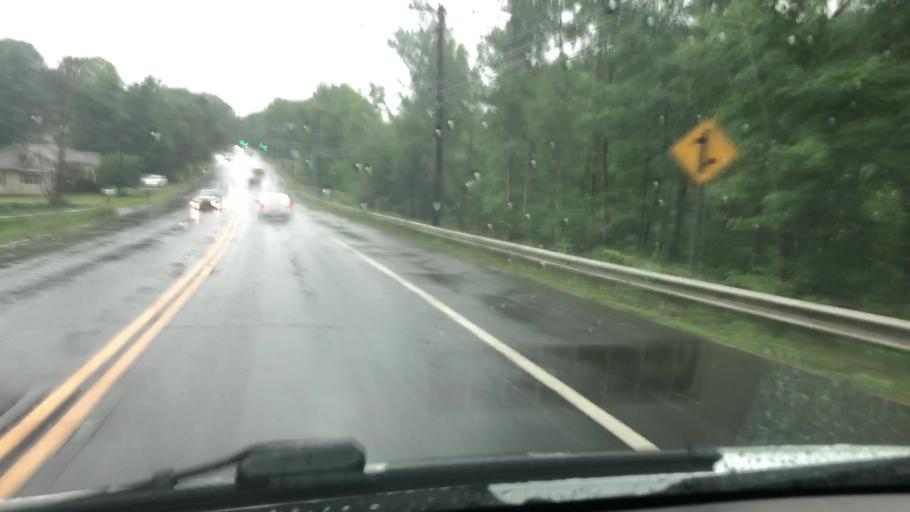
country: US
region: Massachusetts
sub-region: Berkshire County
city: Lanesborough
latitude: 42.4954
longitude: -73.2006
